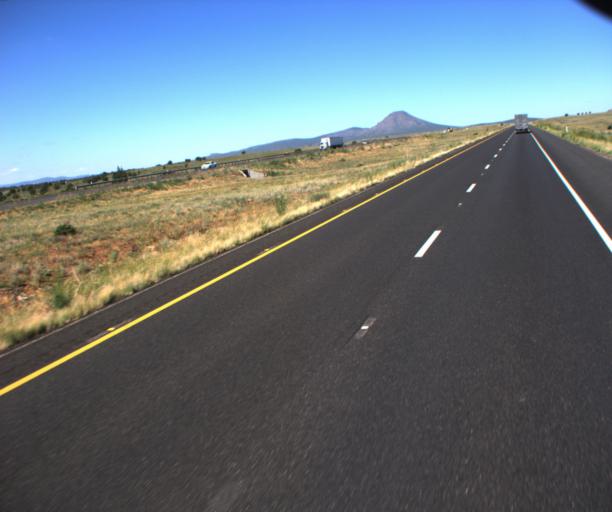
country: US
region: Arizona
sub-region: Yavapai County
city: Paulden
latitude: 35.2343
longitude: -112.6226
